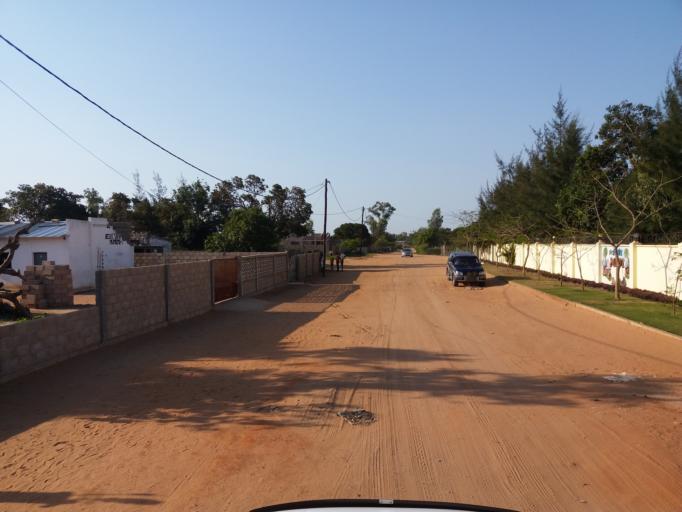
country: MZ
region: Maputo City
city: Maputo
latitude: -25.7643
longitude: 32.6086
